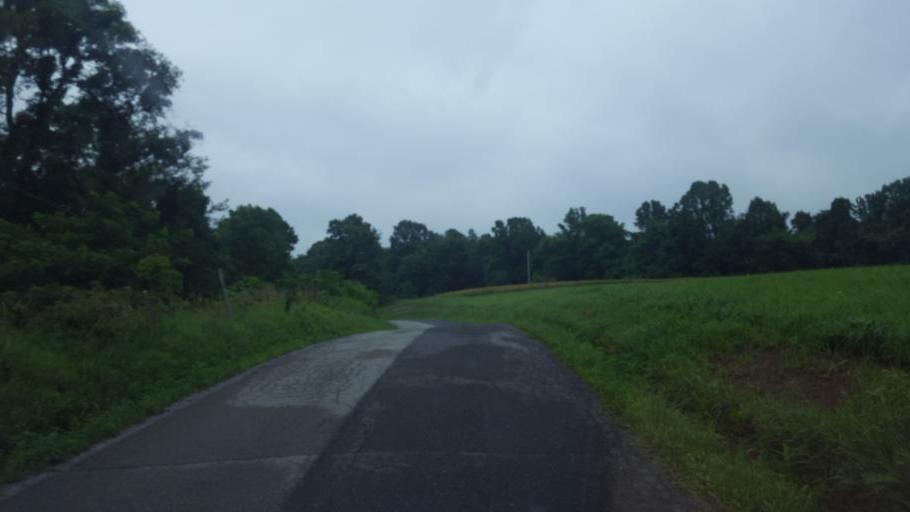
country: US
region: Ohio
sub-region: Columbiana County
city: Salineville
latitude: 40.5679
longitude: -80.8557
